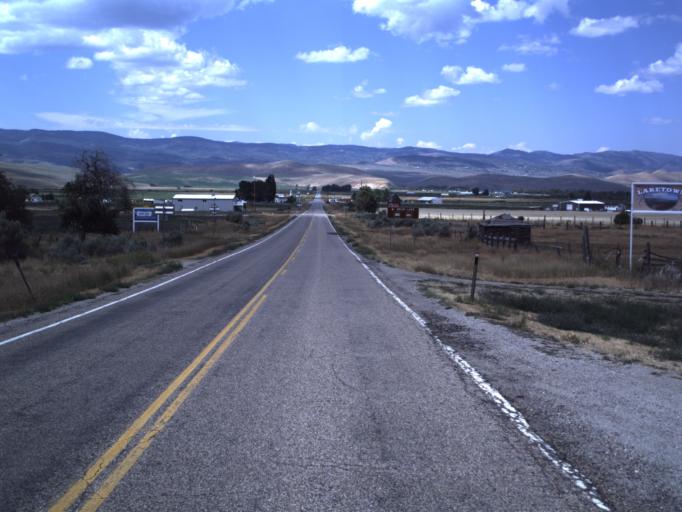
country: US
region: Utah
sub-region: Rich County
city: Randolph
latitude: 41.8281
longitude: -111.3143
